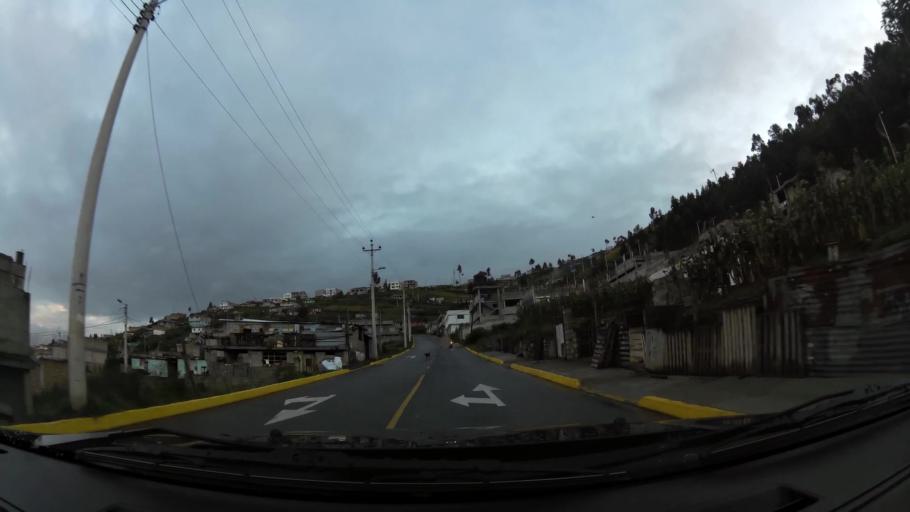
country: EC
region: Pichincha
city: Quito
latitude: -0.0947
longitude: -78.5308
